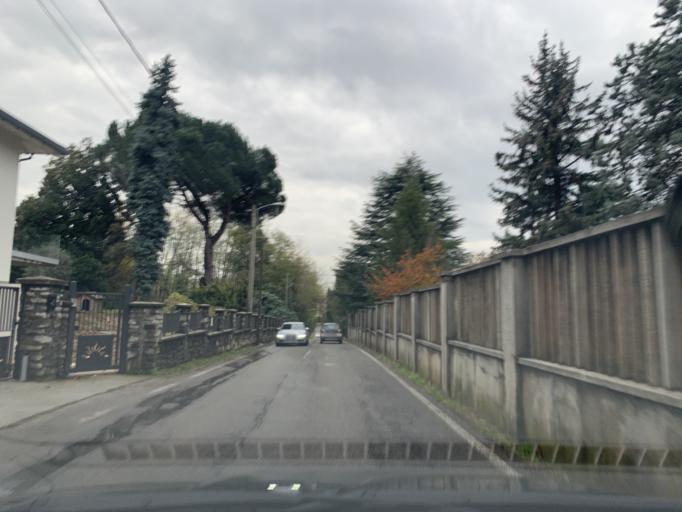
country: IT
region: Lombardy
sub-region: Provincia di Como
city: Puginate
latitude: 45.7165
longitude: 9.0538
